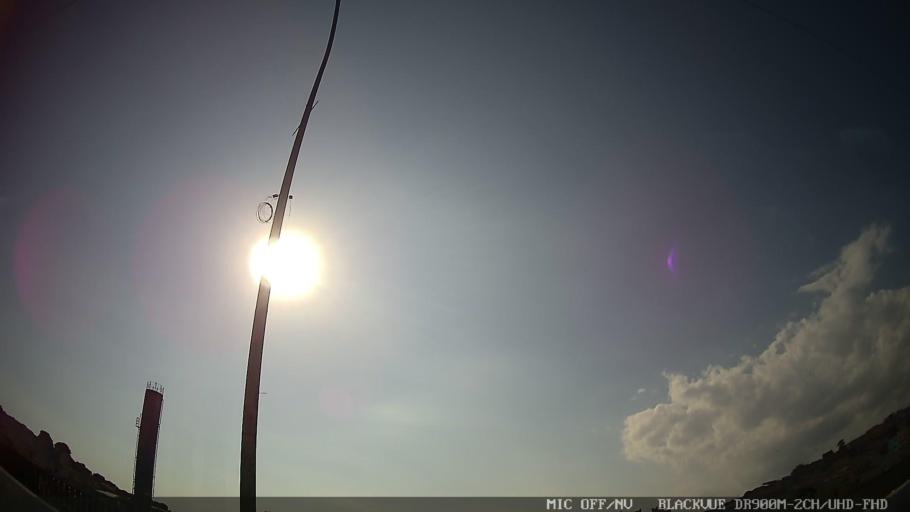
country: BR
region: Sao Paulo
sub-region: Ferraz De Vasconcelos
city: Ferraz de Vasconcelos
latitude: -23.5431
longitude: -46.4105
